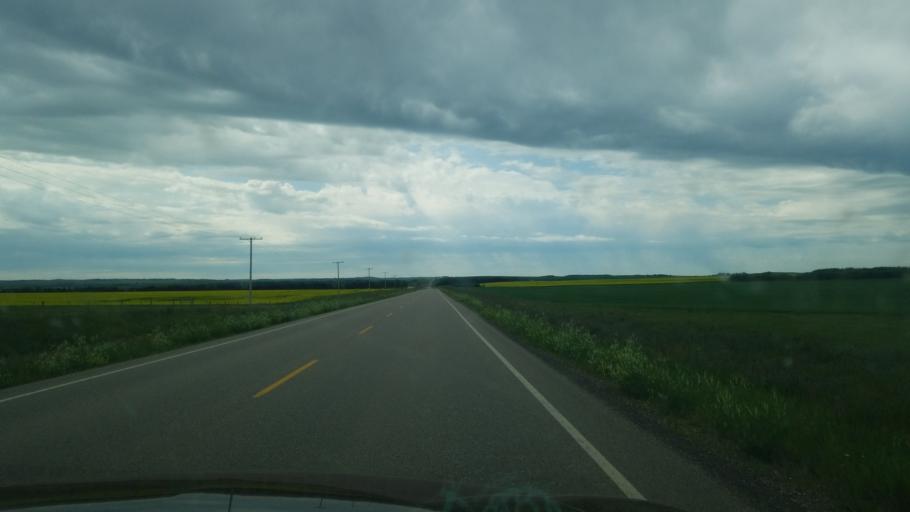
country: CA
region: Saskatchewan
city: Unity
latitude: 52.9580
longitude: -109.3426
